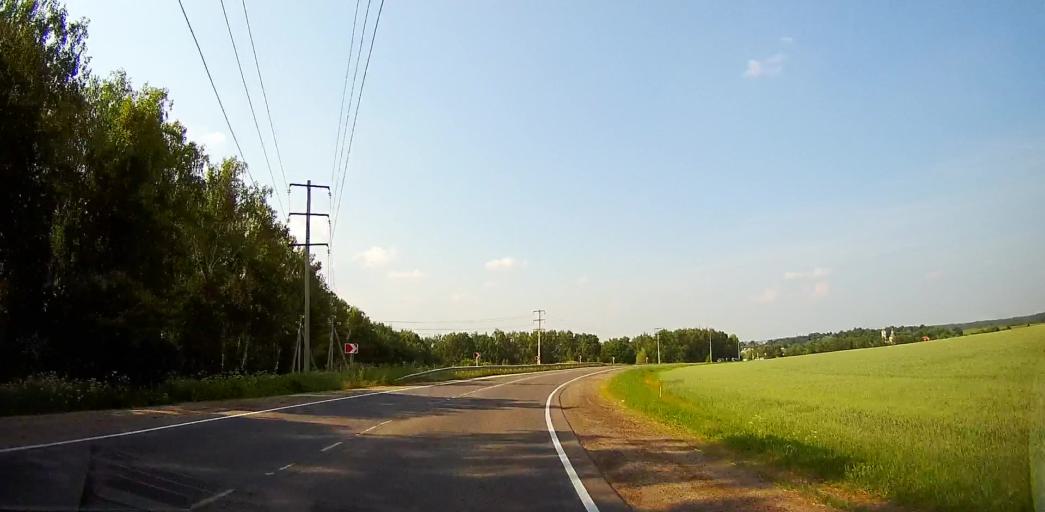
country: RU
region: Moskovskaya
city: Barybino
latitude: 55.2878
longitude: 37.9130
